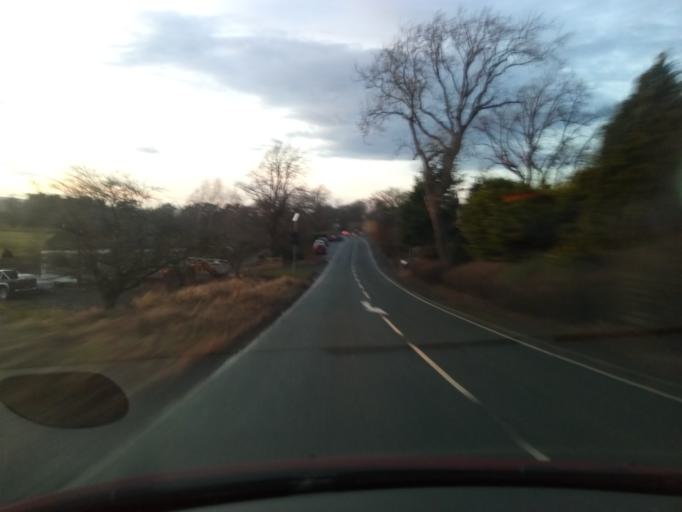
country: GB
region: England
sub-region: Northumberland
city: Otterburn
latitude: 55.2303
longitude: -2.1732
